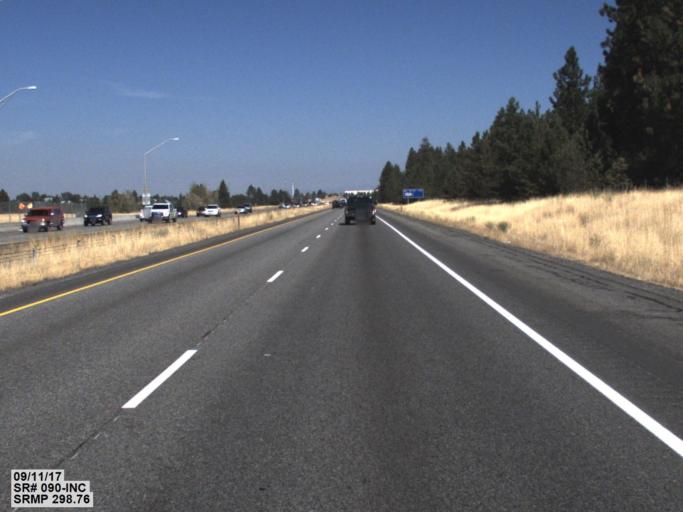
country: US
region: Washington
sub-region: Spokane County
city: Otis Orchards-East Farms
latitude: 47.6908
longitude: -117.0624
